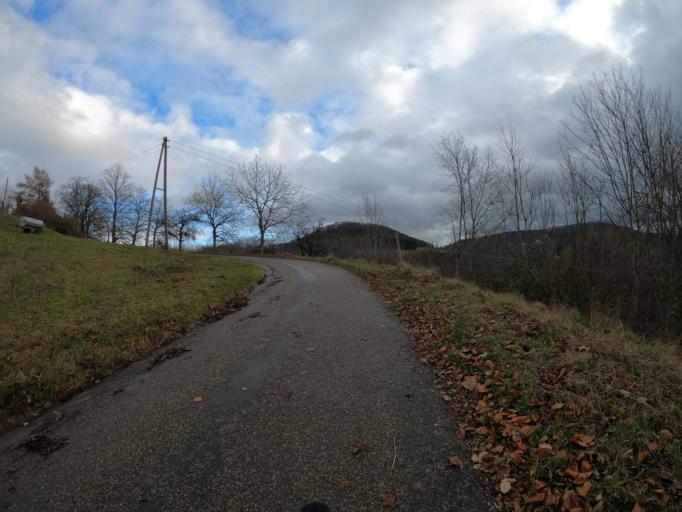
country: DE
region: Baden-Wuerttemberg
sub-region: Regierungsbezirk Stuttgart
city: Waldstetten
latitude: 48.7572
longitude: 9.8393
